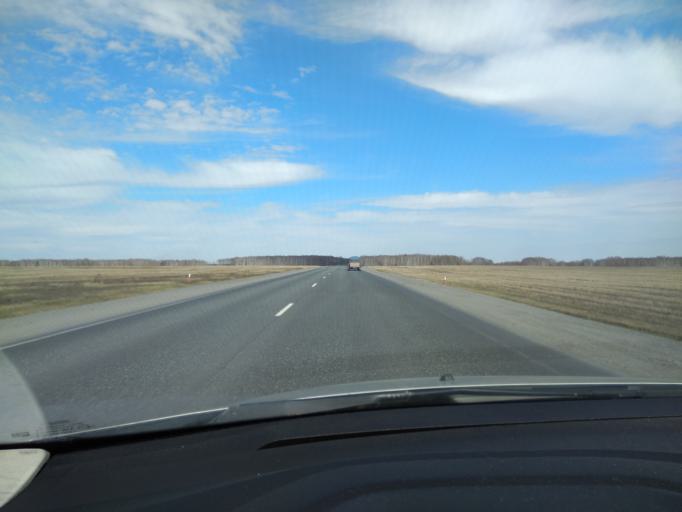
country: RU
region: Sverdlovsk
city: Pyshma
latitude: 56.9219
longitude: 63.1409
